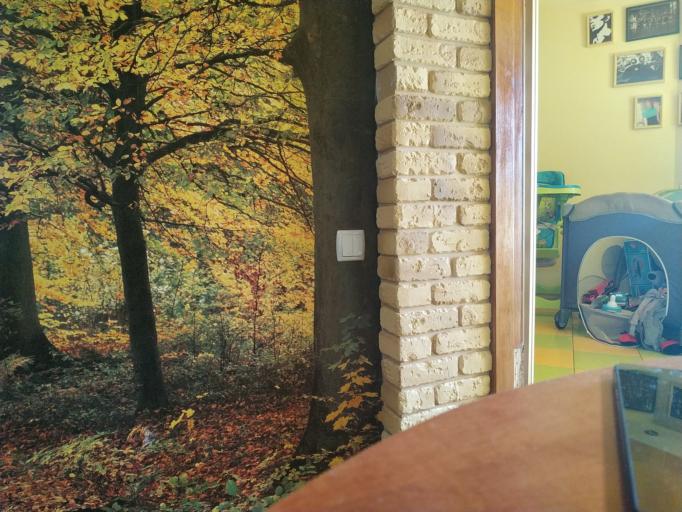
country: RU
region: Tverskaya
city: Torzhok
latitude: 57.0819
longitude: 35.0031
